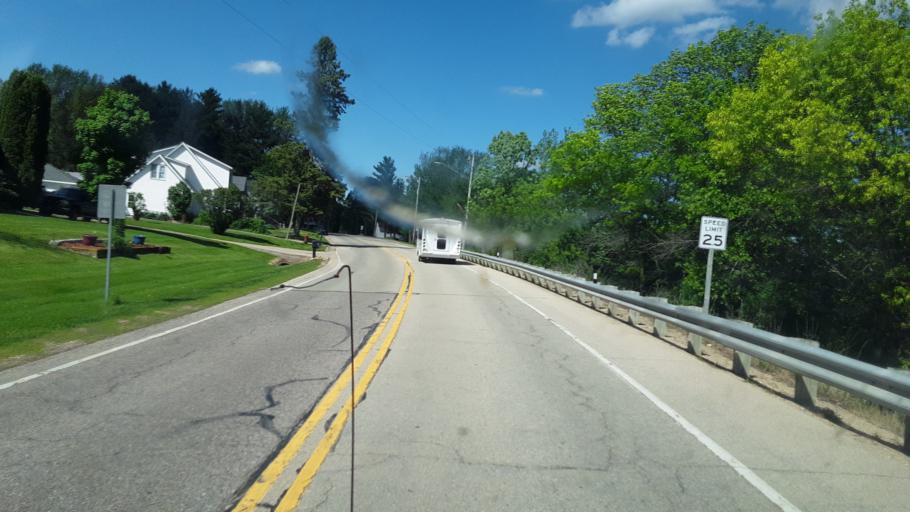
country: US
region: Wisconsin
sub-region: Vernon County
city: Hillsboro
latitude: 43.5209
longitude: -90.2006
